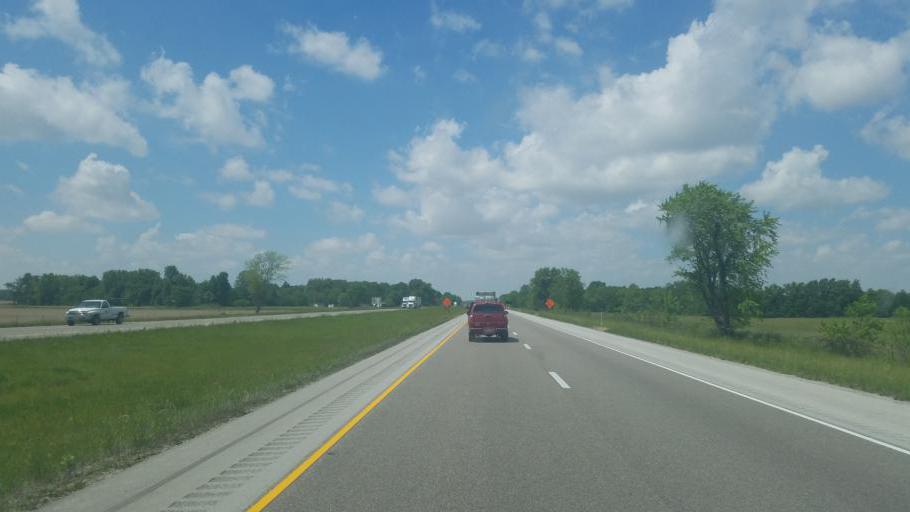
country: US
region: Illinois
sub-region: Cumberland County
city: Toledo
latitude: 39.2253
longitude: -88.2286
